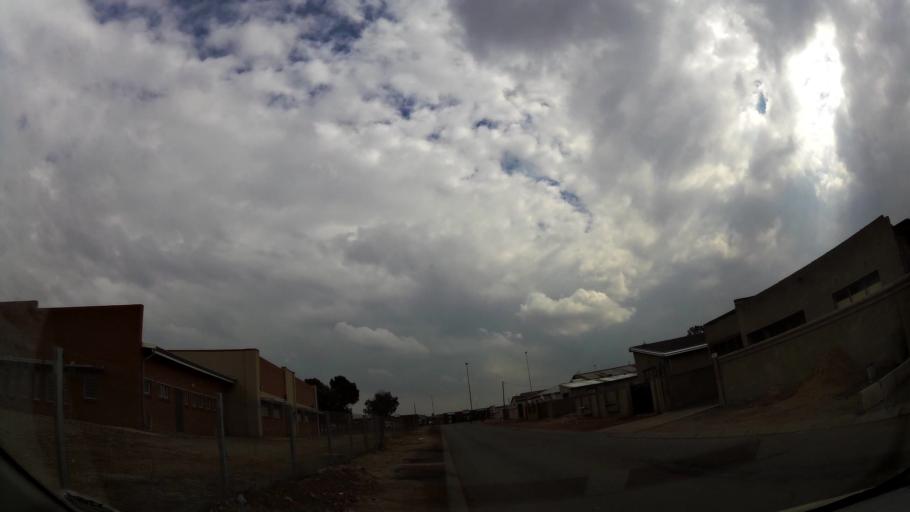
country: ZA
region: Gauteng
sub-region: Ekurhuleni Metropolitan Municipality
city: Germiston
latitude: -26.3878
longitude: 28.1629
